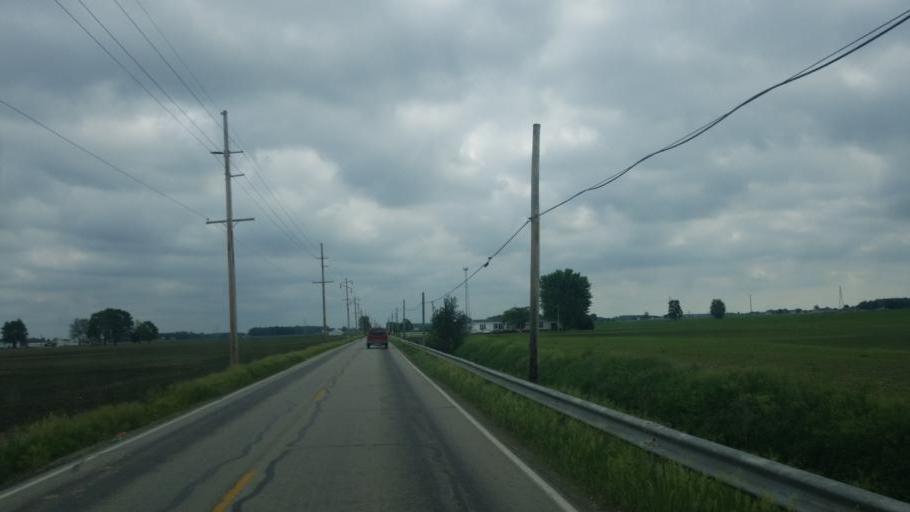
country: US
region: Indiana
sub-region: Elkhart County
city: Nappanee
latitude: 41.4185
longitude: -86.0013
